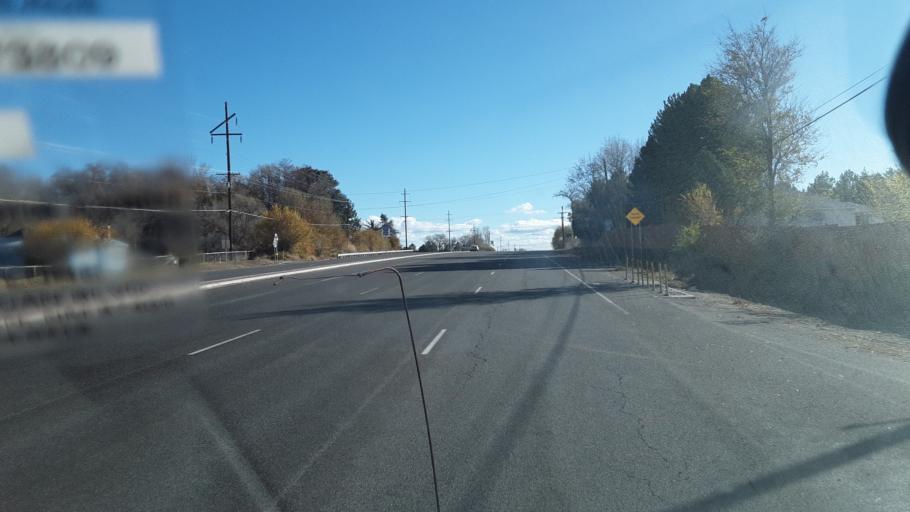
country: US
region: New Mexico
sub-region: San Juan County
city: Lee Acres
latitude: 36.7010
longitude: -108.0577
